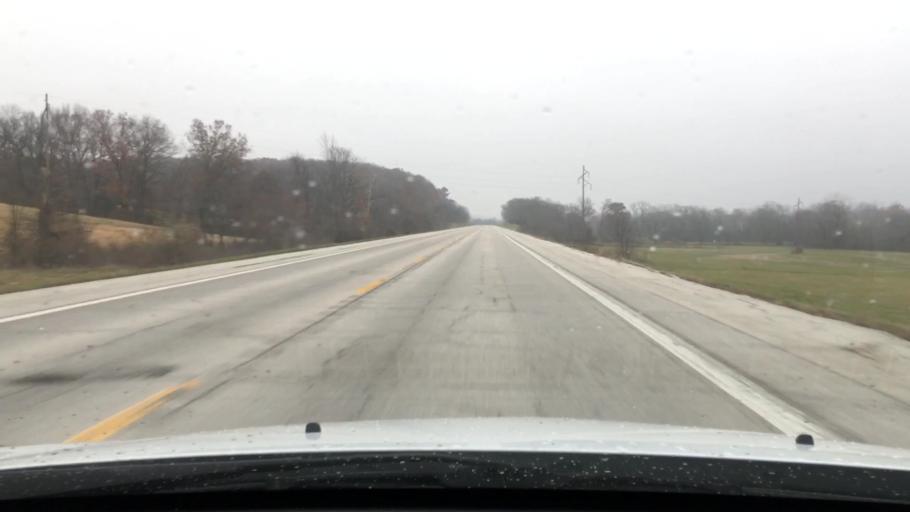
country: US
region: Missouri
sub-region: Pike County
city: Bowling Green
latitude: 39.3745
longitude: -91.1613
